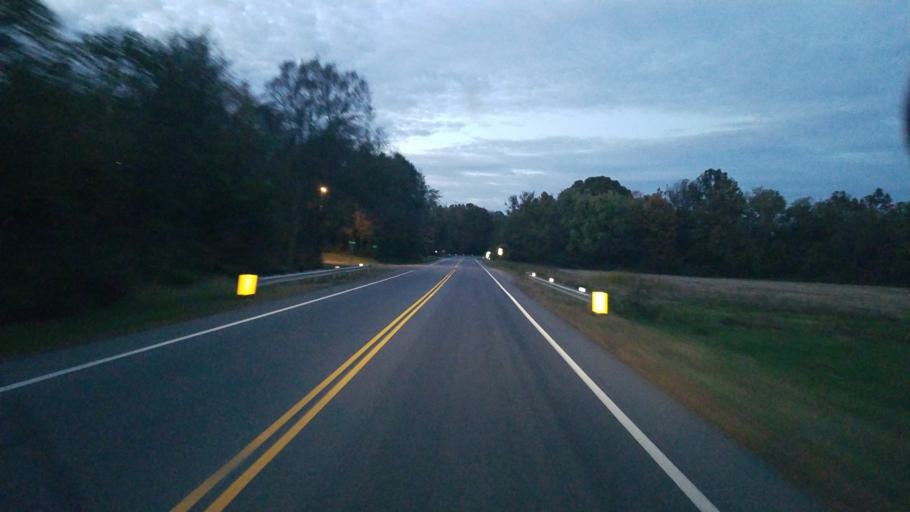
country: US
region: Ohio
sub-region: Scioto County
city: West Portsmouth
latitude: 38.7907
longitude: -83.0145
